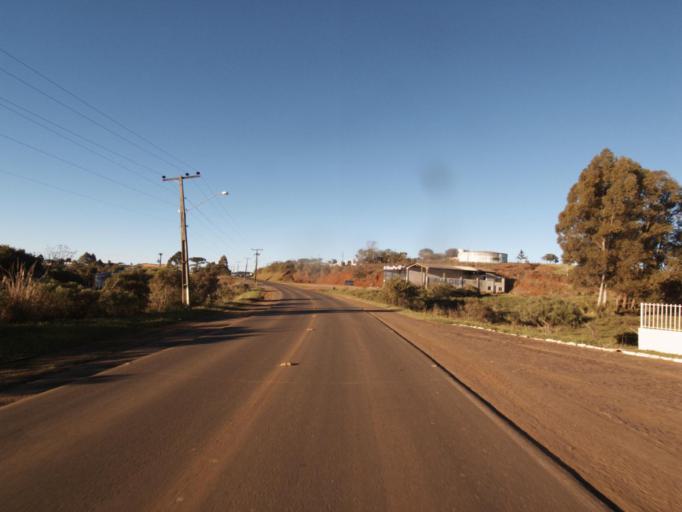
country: AR
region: Misiones
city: Bernardo de Irigoyen
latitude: -26.2696
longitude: -53.6299
